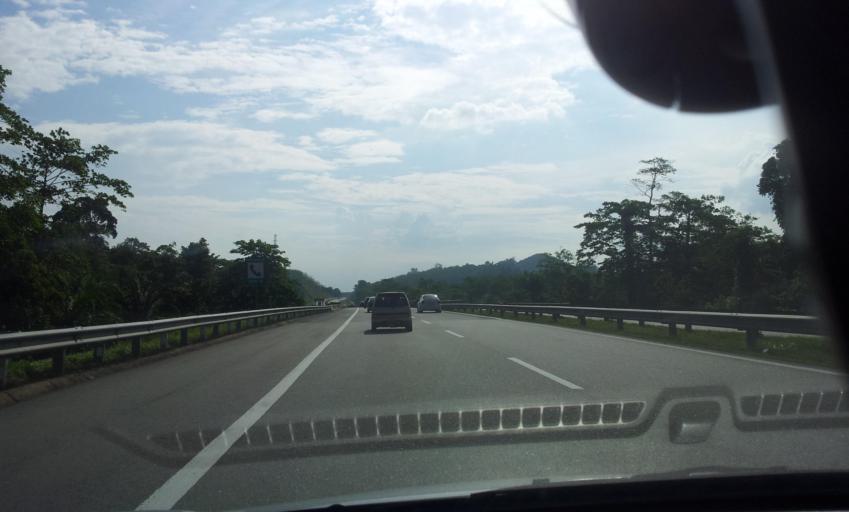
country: MY
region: Pahang
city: Mentekab
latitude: 3.5291
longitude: 102.2190
